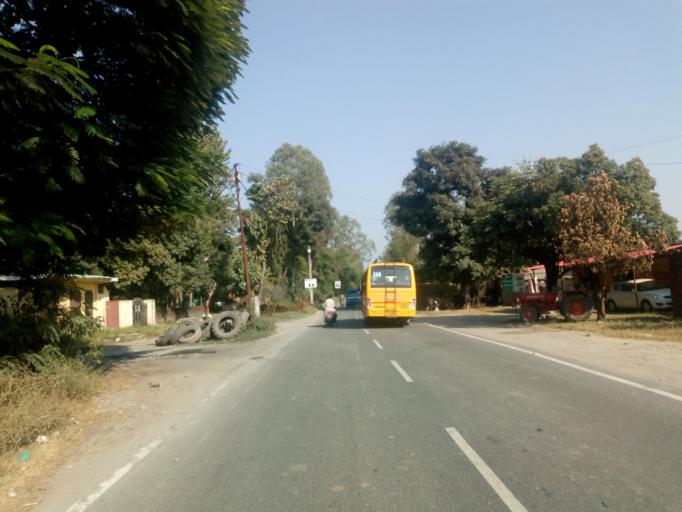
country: IN
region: Uttarakhand
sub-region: Dehradun
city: Harbatpur
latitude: 30.4415
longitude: 77.6946
